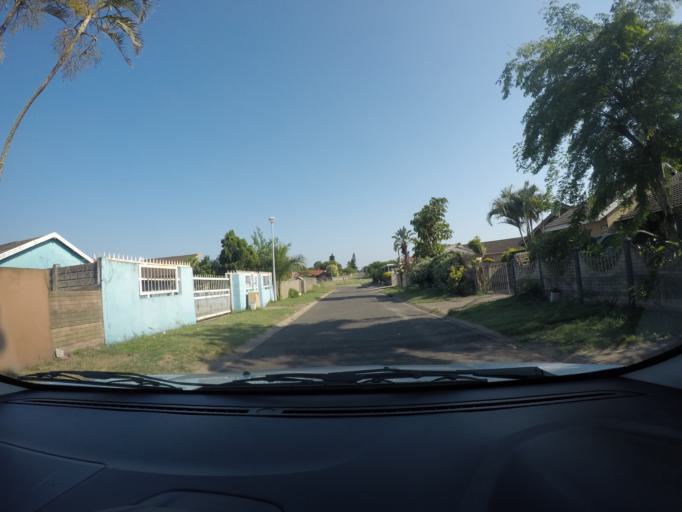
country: ZA
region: KwaZulu-Natal
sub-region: uThungulu District Municipality
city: Richards Bay
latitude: -28.7154
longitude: 32.0324
